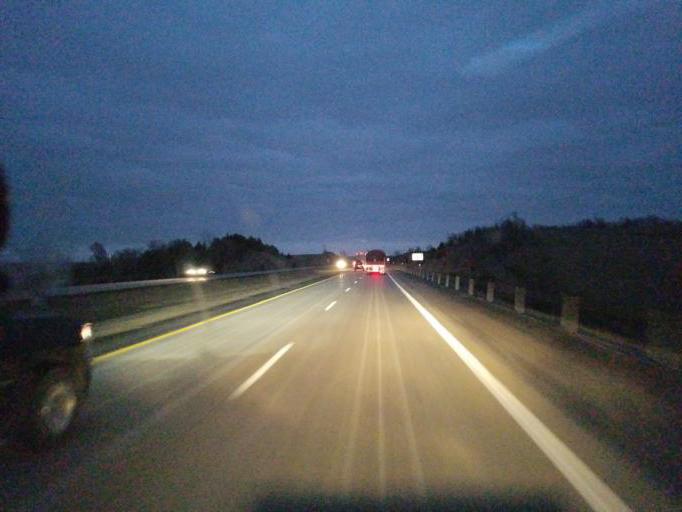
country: US
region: Iowa
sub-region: Cass County
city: Atlantic
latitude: 41.4965
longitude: -94.7756
